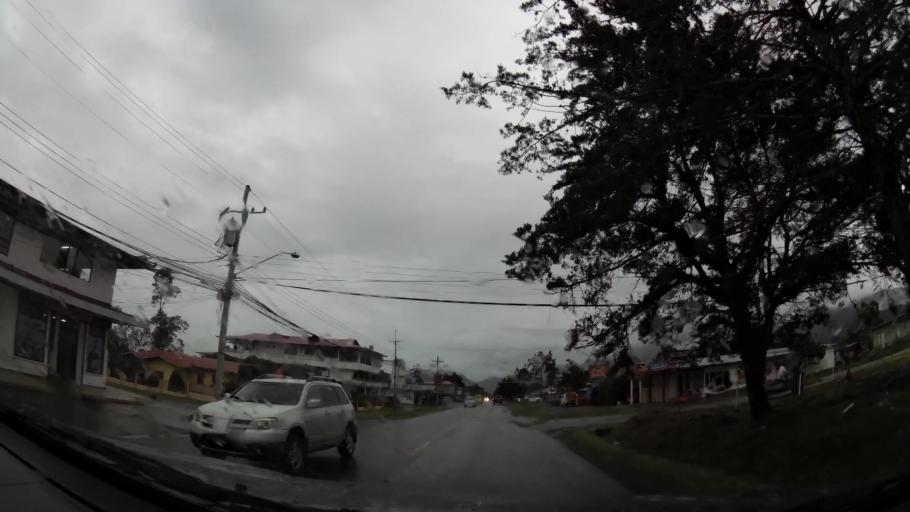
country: PA
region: Chiriqui
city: Volcan
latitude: 8.7823
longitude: -82.6467
